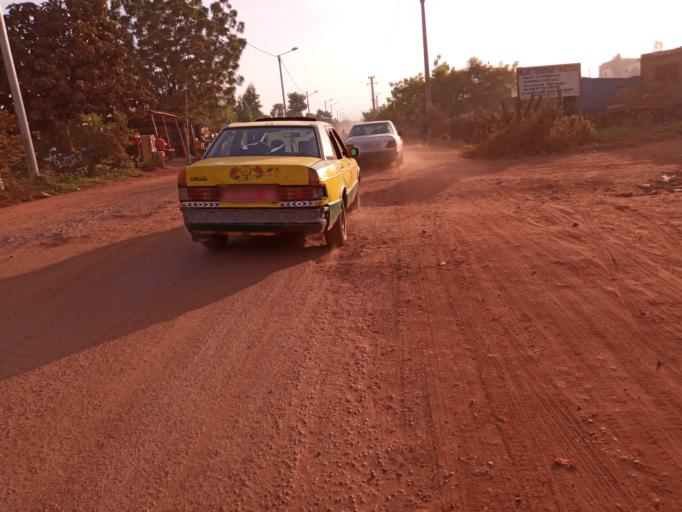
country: ML
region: Bamako
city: Bamako
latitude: 12.6348
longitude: -7.9338
